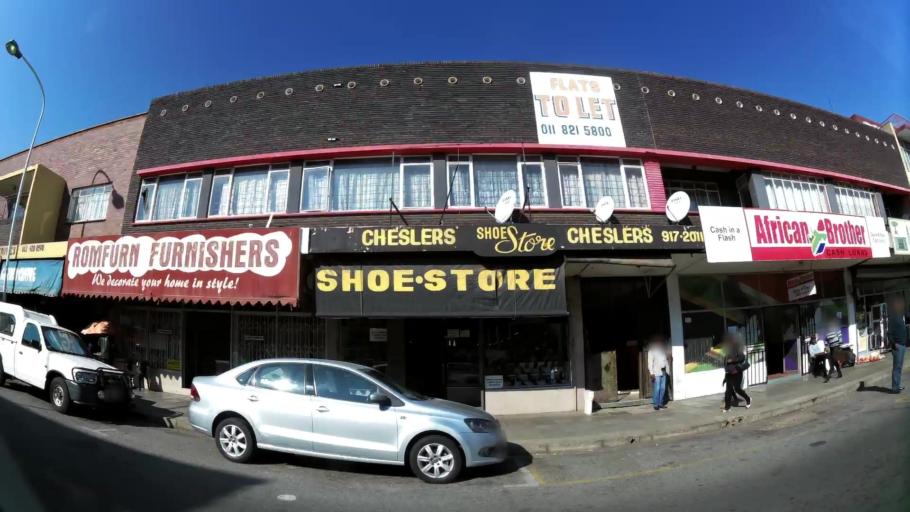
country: ZA
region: Gauteng
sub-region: Ekurhuleni Metropolitan Municipality
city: Boksburg
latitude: -26.2234
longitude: 28.2553
